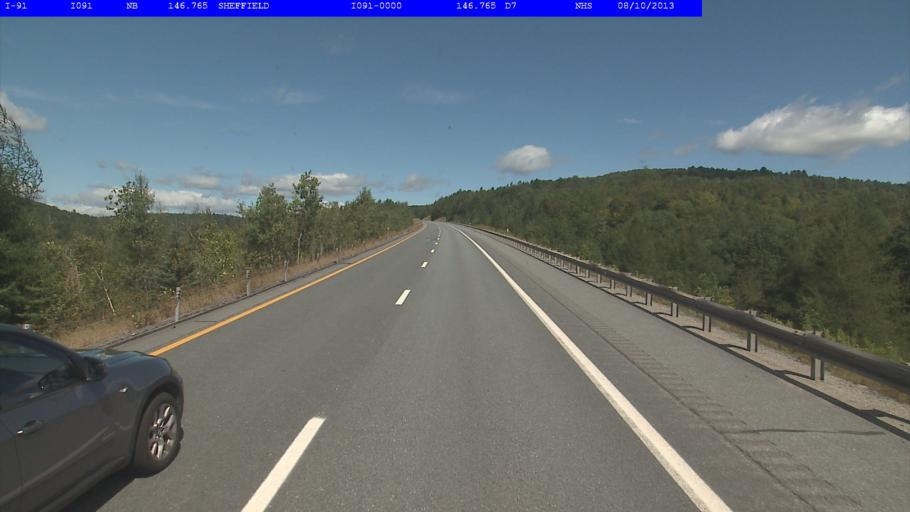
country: US
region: Vermont
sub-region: Caledonia County
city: Lyndonville
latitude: 44.6195
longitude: -72.1217
